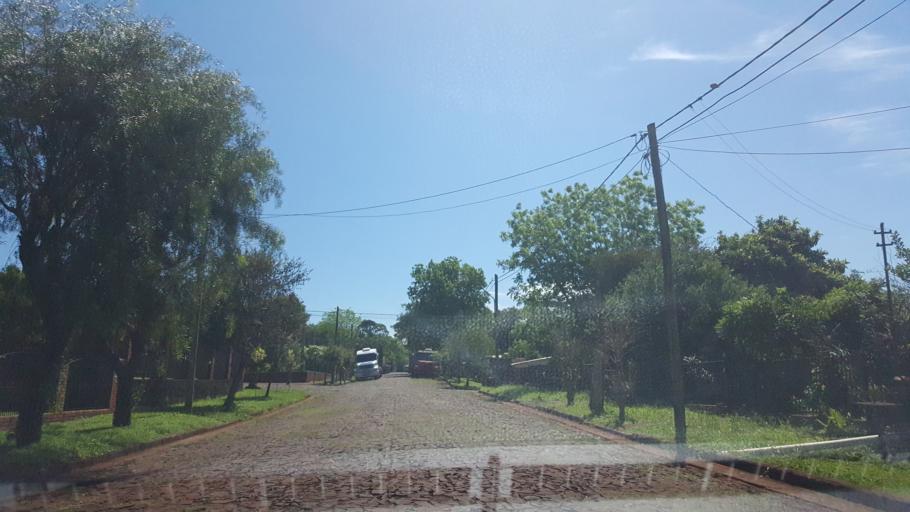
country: AR
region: Misiones
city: Capiovi
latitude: -26.9302
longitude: -55.0609
